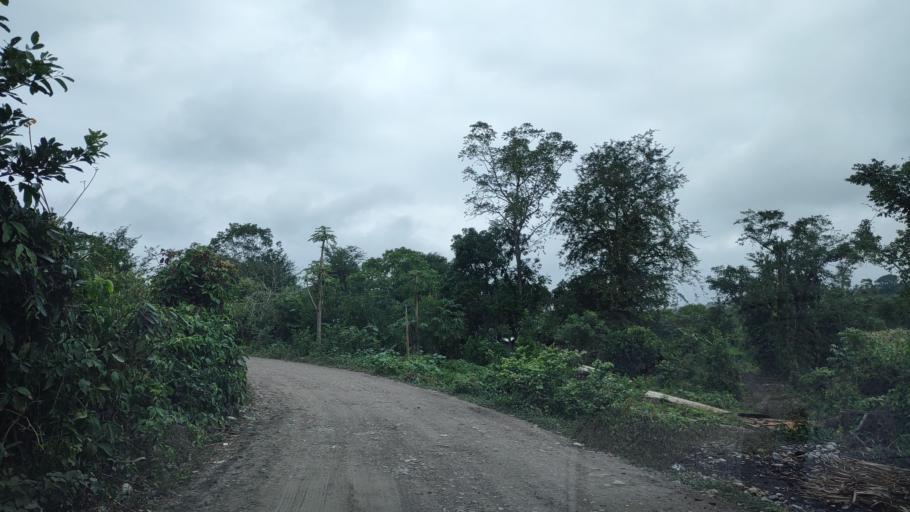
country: MX
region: Veracruz
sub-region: Coatzintla
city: Manuel Maria Contreras
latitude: 20.4046
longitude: -97.4529
